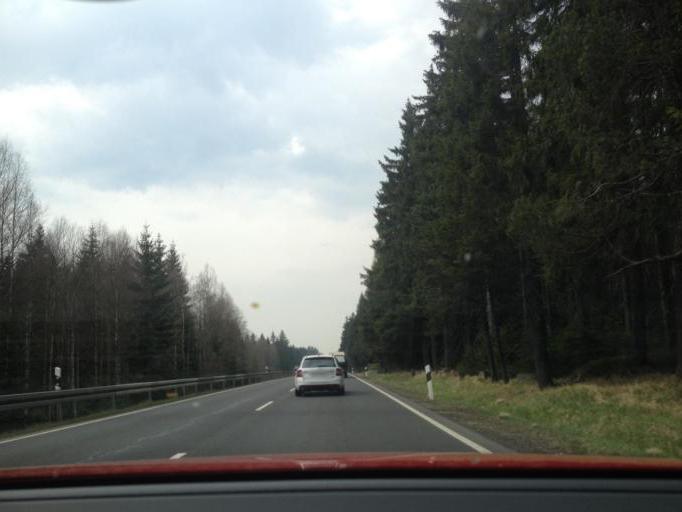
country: DE
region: Bavaria
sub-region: Upper Franconia
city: Fichtelberg
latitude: 50.0218
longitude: 11.8665
